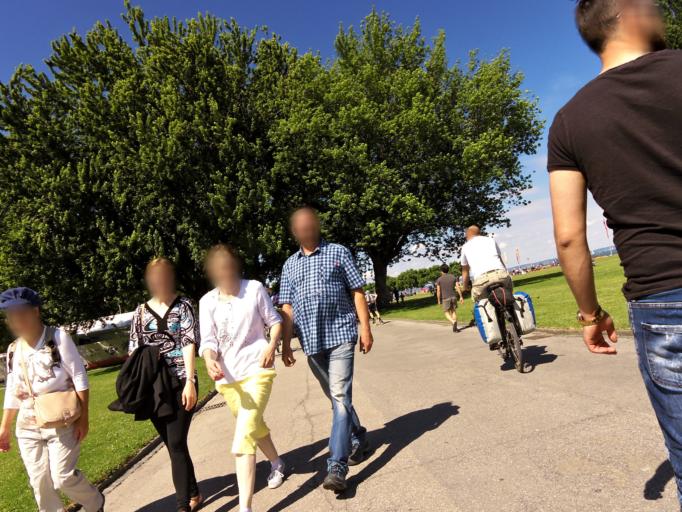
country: CH
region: Thurgau
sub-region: Arbon District
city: Arbon
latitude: 47.5146
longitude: 9.4382
